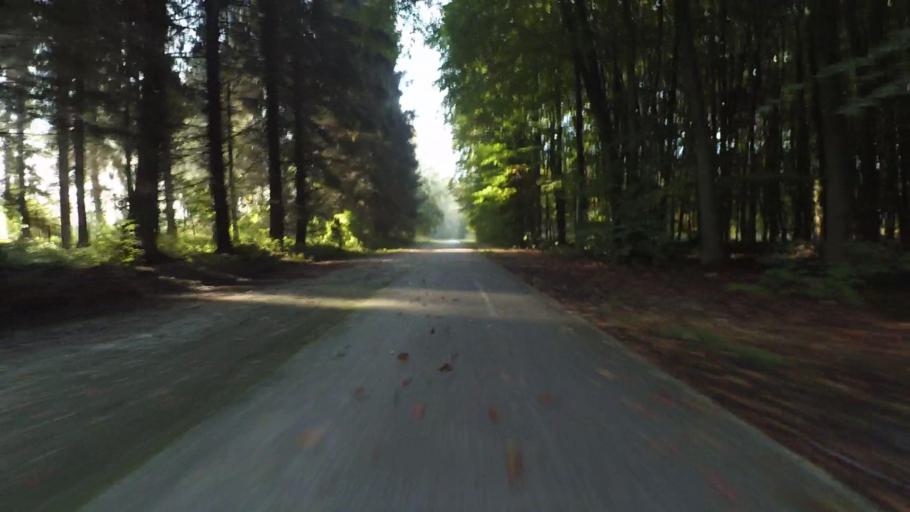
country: NL
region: Flevoland
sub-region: Gemeente Zeewolde
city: Zeewolde
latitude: 52.2804
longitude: 5.5263
